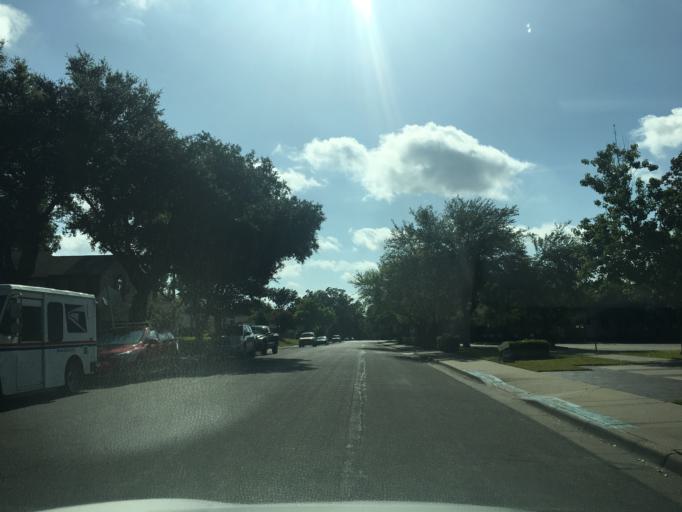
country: US
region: Texas
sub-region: Dallas County
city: Highland Park
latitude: 32.8329
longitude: -96.7548
